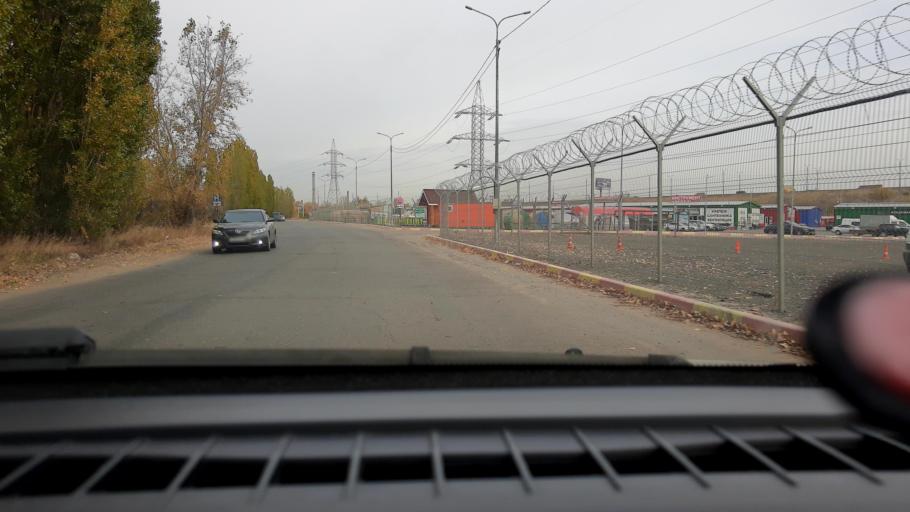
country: RU
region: Nizjnij Novgorod
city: Nizhniy Novgorod
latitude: 56.2518
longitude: 43.9370
